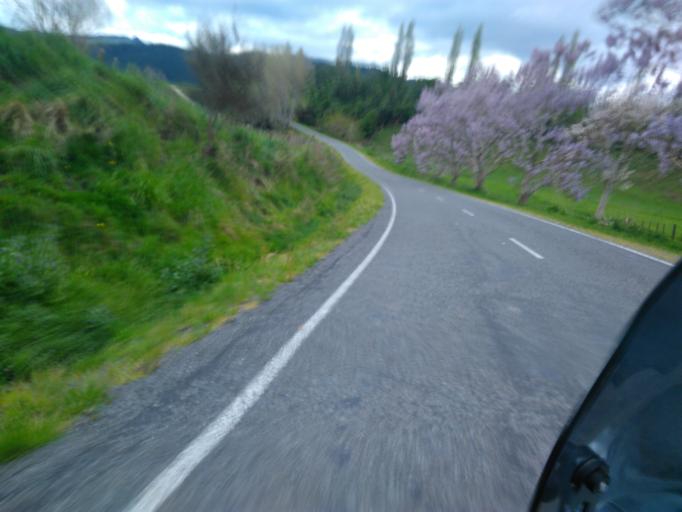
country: NZ
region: Hawke's Bay
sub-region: Wairoa District
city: Wairoa
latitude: -38.8805
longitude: 177.4974
